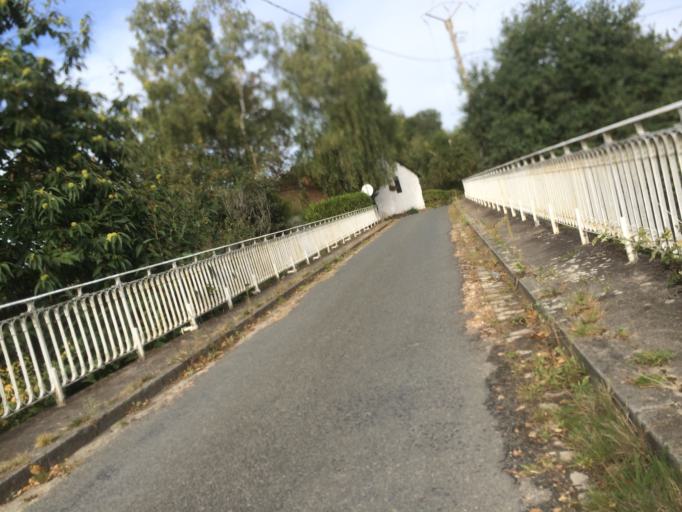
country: FR
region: Ile-de-France
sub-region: Departement des Yvelines
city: Bonnelles
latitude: 48.6307
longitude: 2.0423
